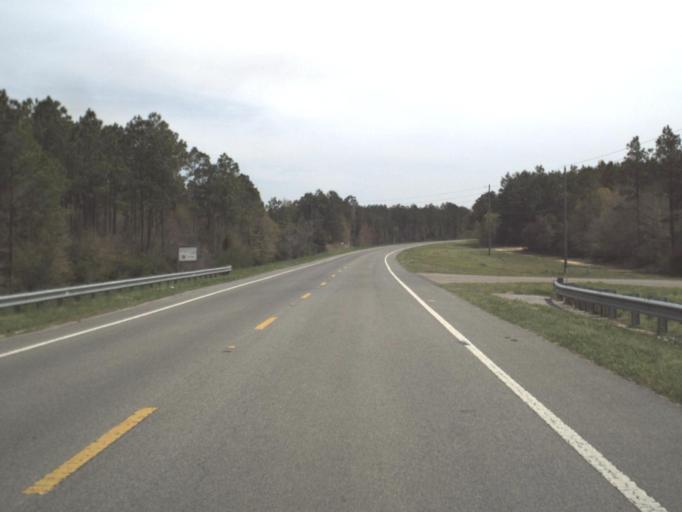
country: US
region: Alabama
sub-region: Geneva County
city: Geneva
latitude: 30.9497
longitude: -85.8391
